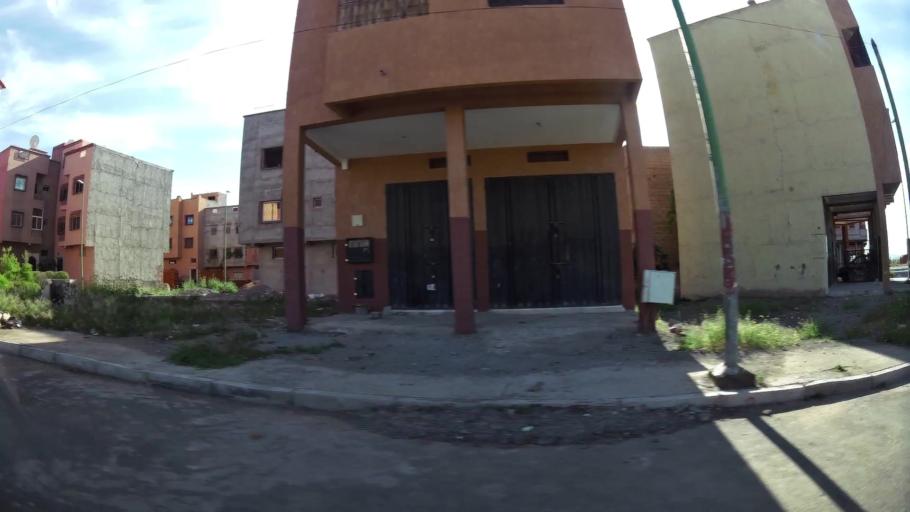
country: MA
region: Marrakech-Tensift-Al Haouz
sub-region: Marrakech
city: Marrakesh
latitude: 31.6891
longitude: -8.0635
